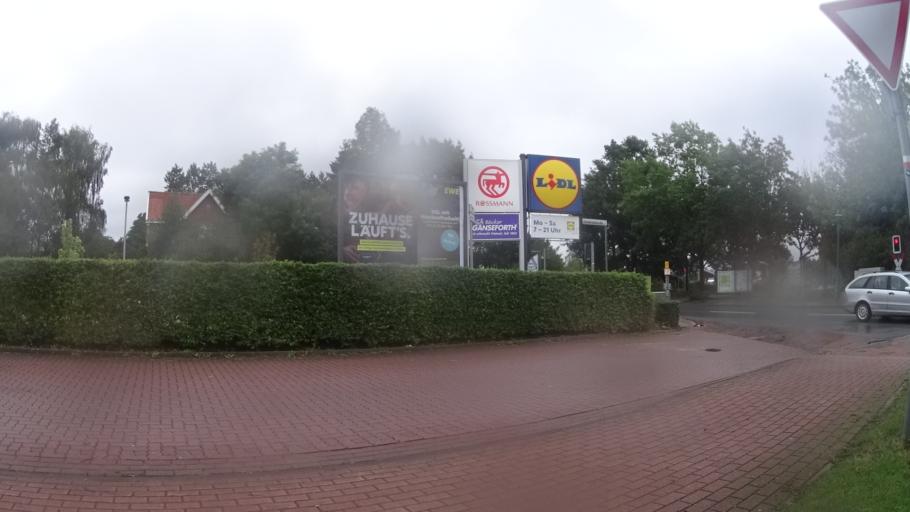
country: DE
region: Lower Saxony
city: Bunde
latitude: 53.1830
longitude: 7.2637
